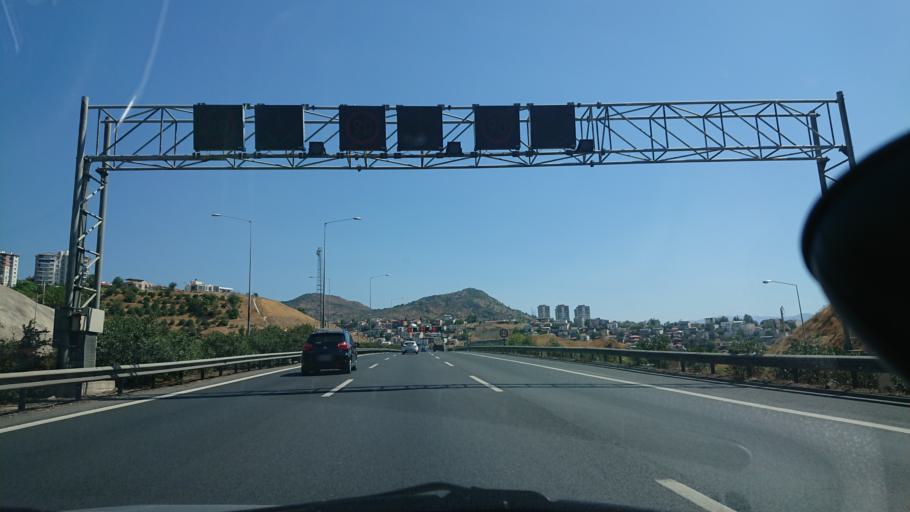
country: TR
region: Izmir
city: Karsiyaka
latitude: 38.4863
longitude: 27.1296
